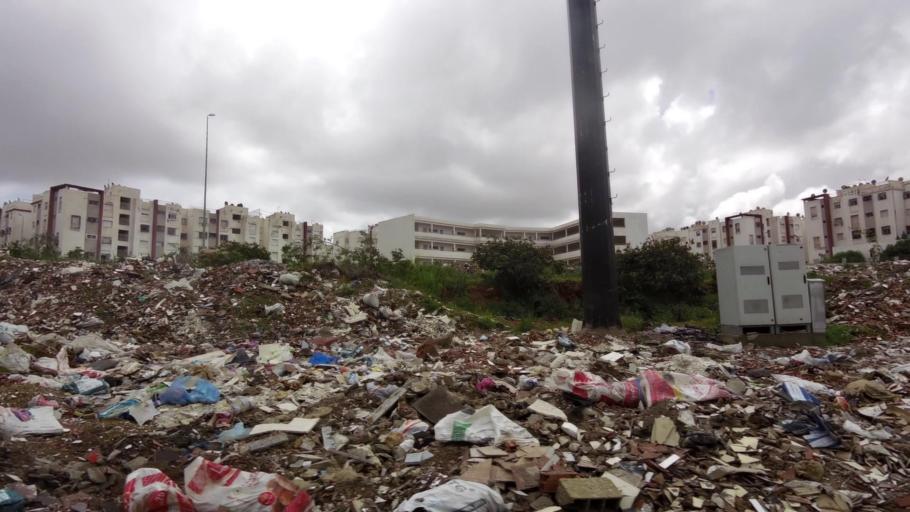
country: MA
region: Grand Casablanca
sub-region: Casablanca
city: Casablanca
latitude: 33.5434
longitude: -7.6969
